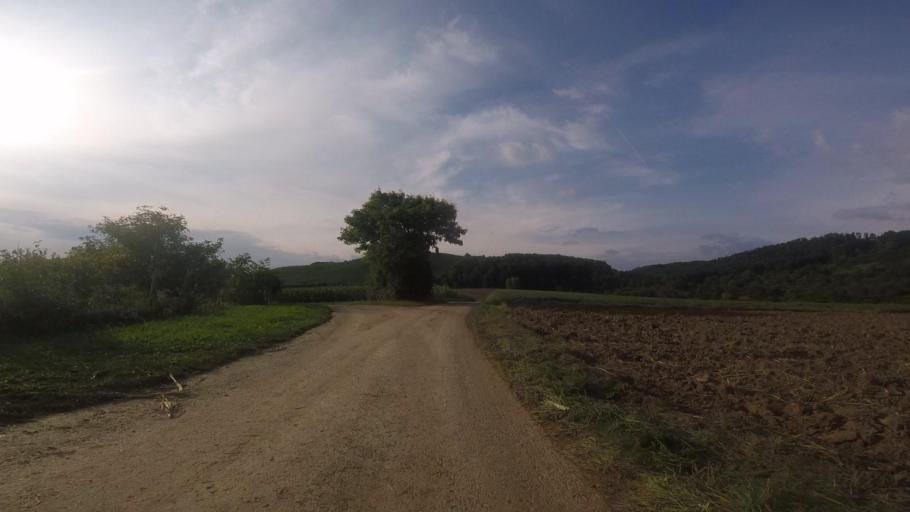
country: DE
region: Baden-Wuerttemberg
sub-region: Regierungsbezirk Stuttgart
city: Aspach
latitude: 48.9945
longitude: 9.3827
